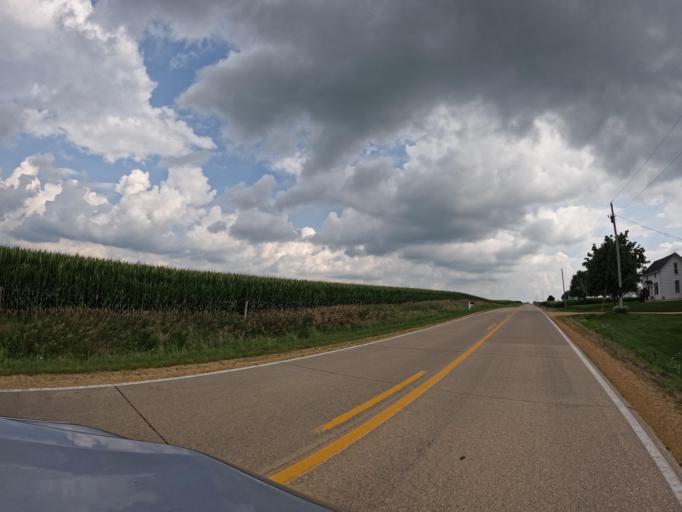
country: US
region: Iowa
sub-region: Clinton County
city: De Witt
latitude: 41.7751
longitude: -90.4131
